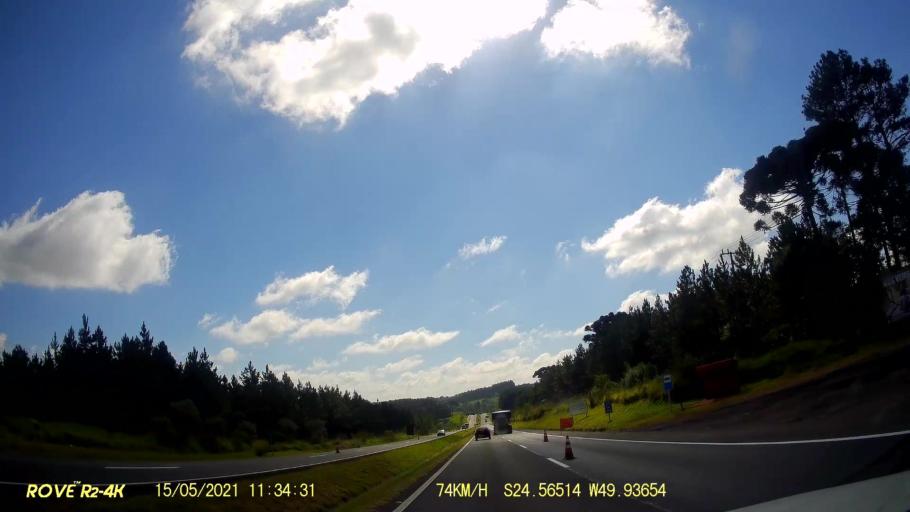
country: BR
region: Parana
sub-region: Pirai Do Sul
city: Pirai do Sul
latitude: -24.5652
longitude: -49.9366
